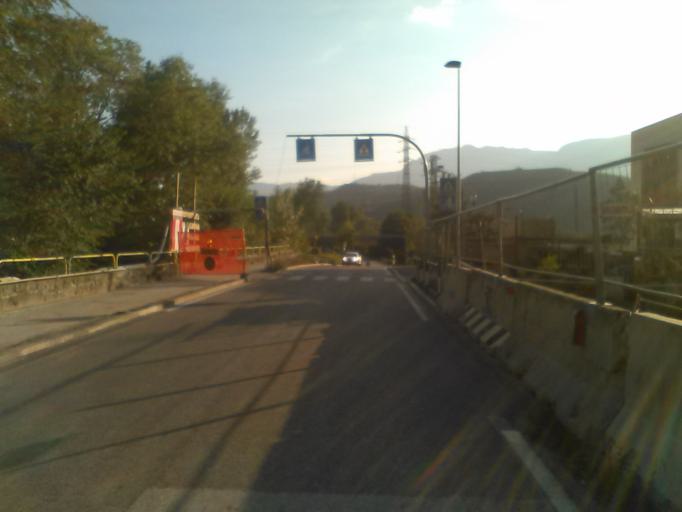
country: IT
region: Trentino-Alto Adige
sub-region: Bolzano
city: Bolzano
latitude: 46.4797
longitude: 11.3185
